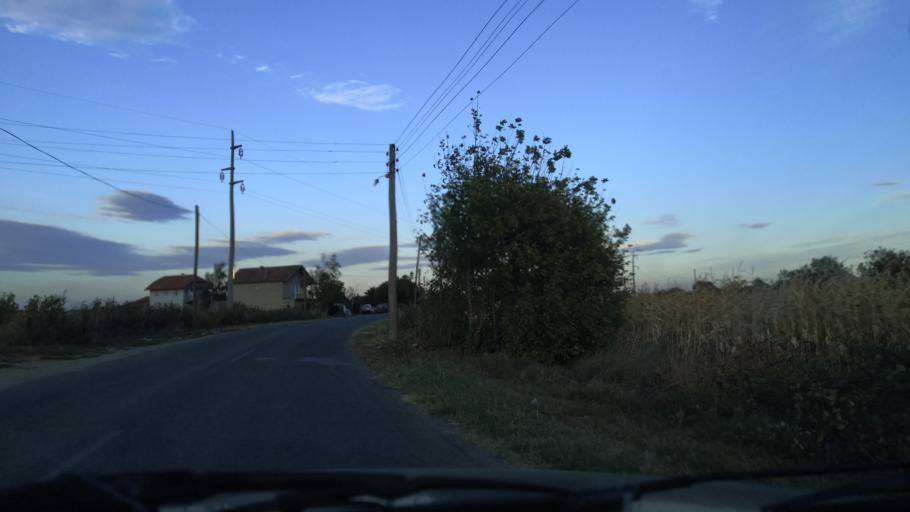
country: RS
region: Central Serbia
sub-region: Borski Okrug
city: Negotin
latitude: 44.2396
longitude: 22.5550
